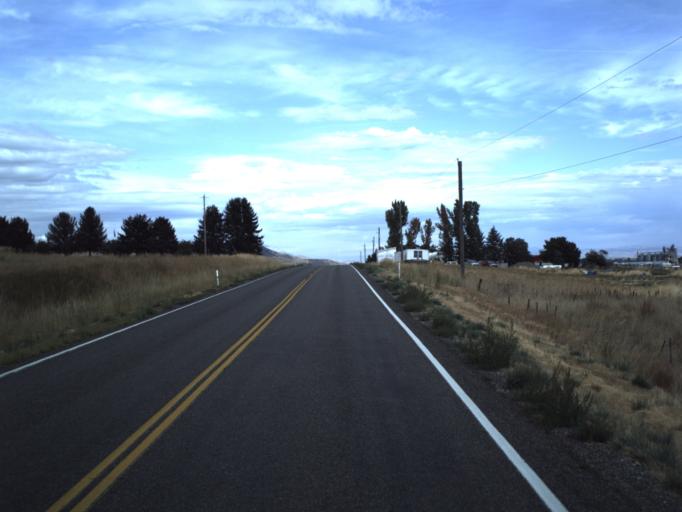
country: US
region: Utah
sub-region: Cache County
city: Benson
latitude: 41.9041
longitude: -111.9517
